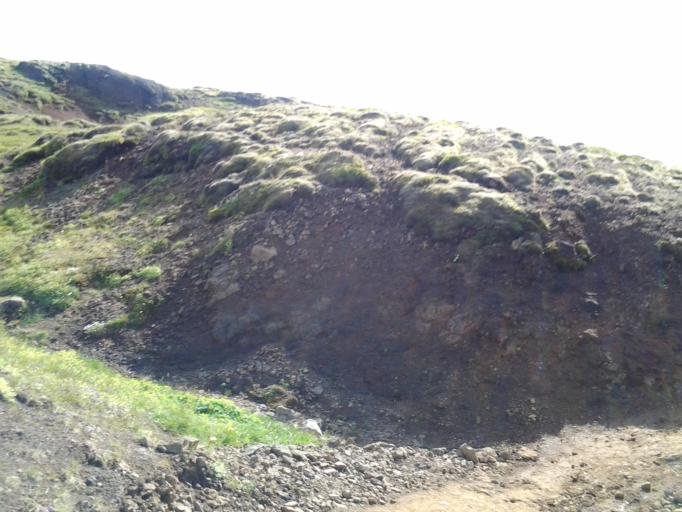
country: IS
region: South
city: Hveragerdi
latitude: 64.0370
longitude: -21.2184
